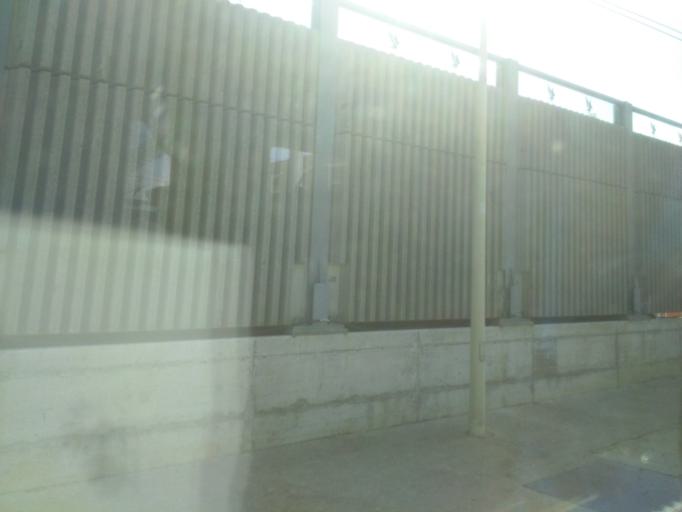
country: IT
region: Lombardy
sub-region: Citta metropolitana di Milano
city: Millepini
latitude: 45.4854
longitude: 9.3268
